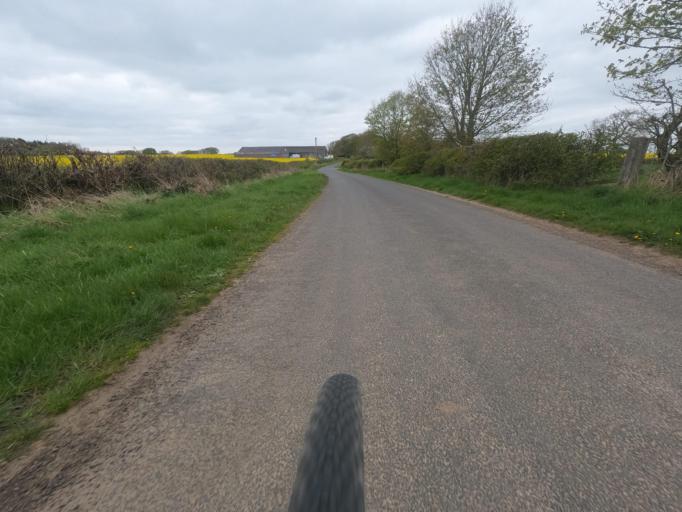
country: GB
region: England
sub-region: Northumberland
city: Horsley
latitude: 55.0602
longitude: -1.8460
